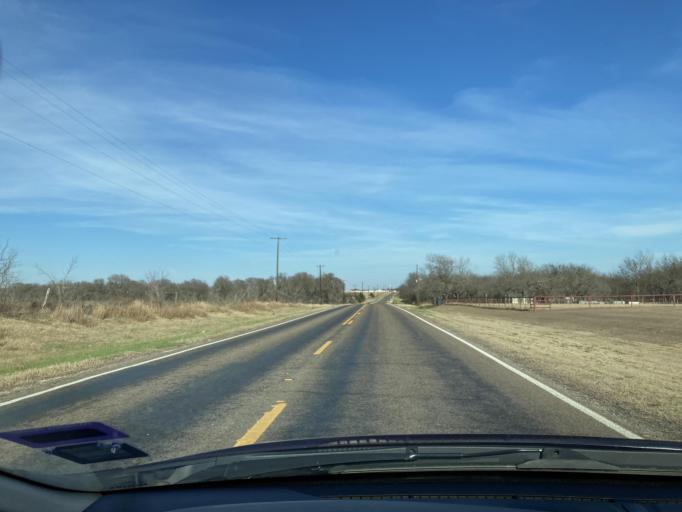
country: US
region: Texas
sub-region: Navarro County
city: Corsicana
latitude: 32.0177
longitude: -96.4233
